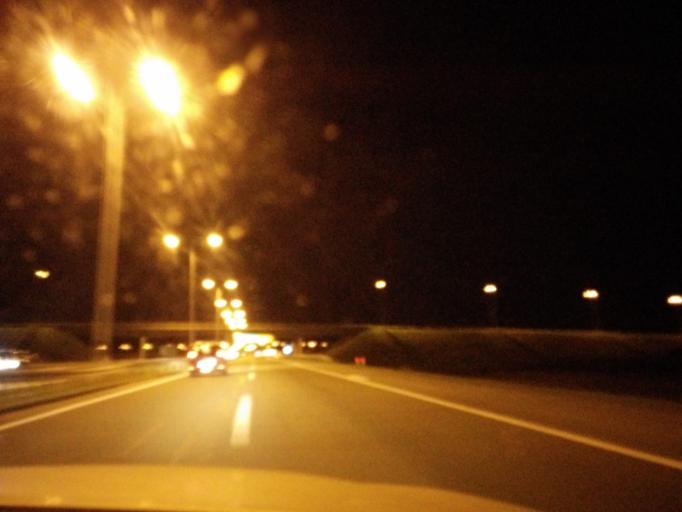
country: RS
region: Autonomna Pokrajina Vojvodina
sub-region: Sremski Okrug
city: Pecinci
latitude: 44.9203
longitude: 19.9608
